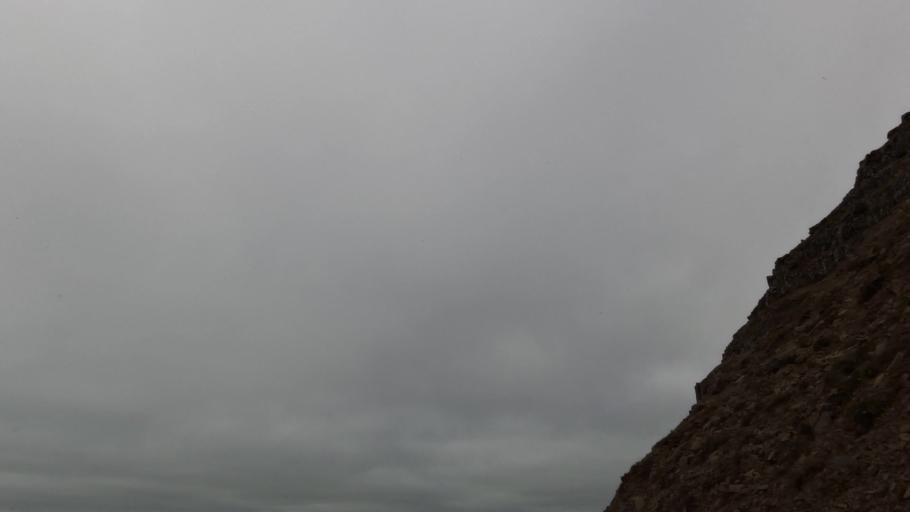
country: IS
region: West
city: Olafsvik
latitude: 65.5099
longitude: -24.5104
